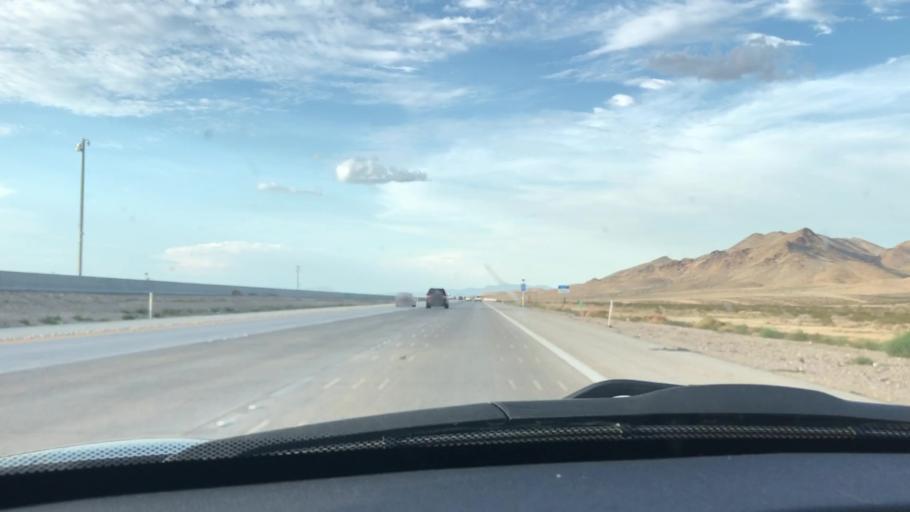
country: US
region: Nevada
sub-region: Clark County
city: Enterprise
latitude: 35.8752
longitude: -115.2378
